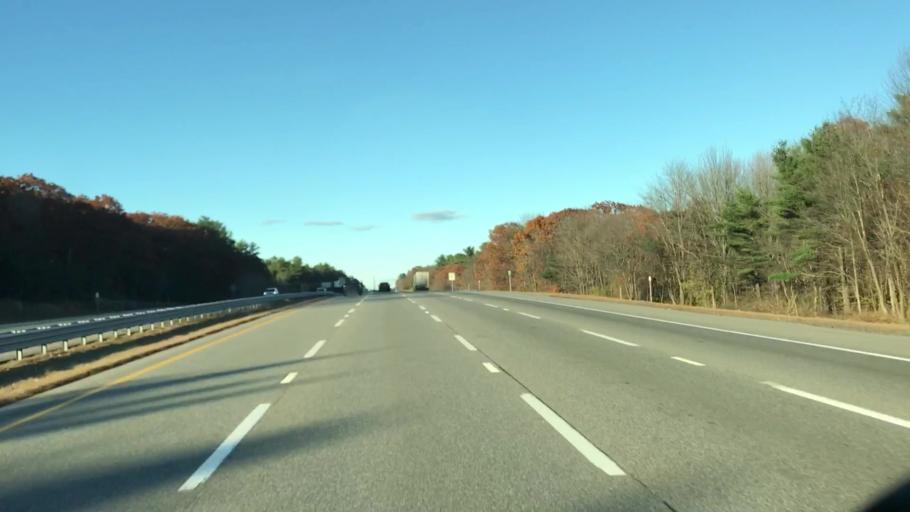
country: US
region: Maine
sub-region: York County
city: York Harbor
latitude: 43.1676
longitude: -70.6532
